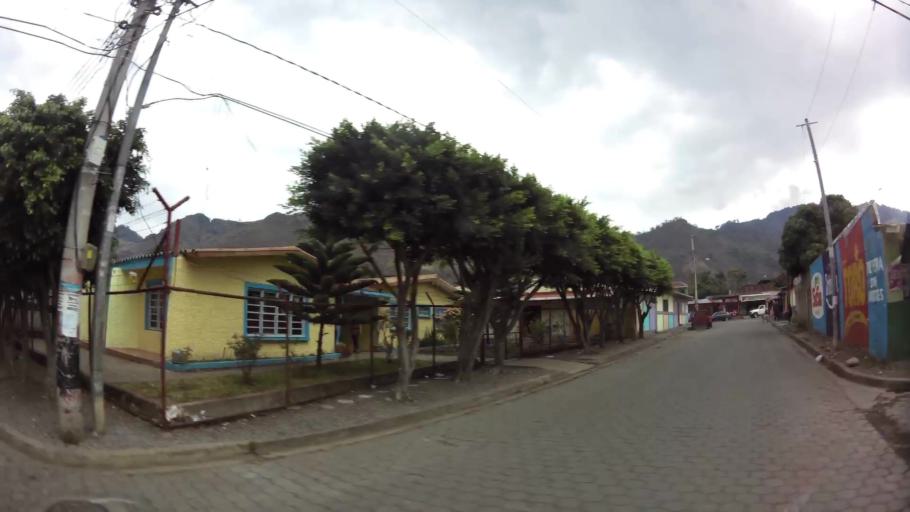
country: NI
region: Jinotega
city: Jinotega
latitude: 13.0944
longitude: -85.9990
